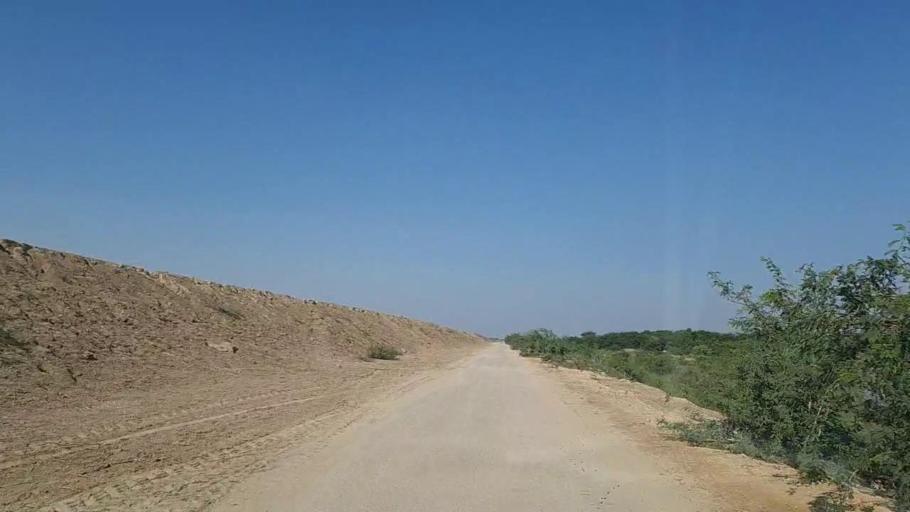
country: PK
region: Sindh
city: Chuhar Jamali
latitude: 24.5684
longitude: 68.0296
